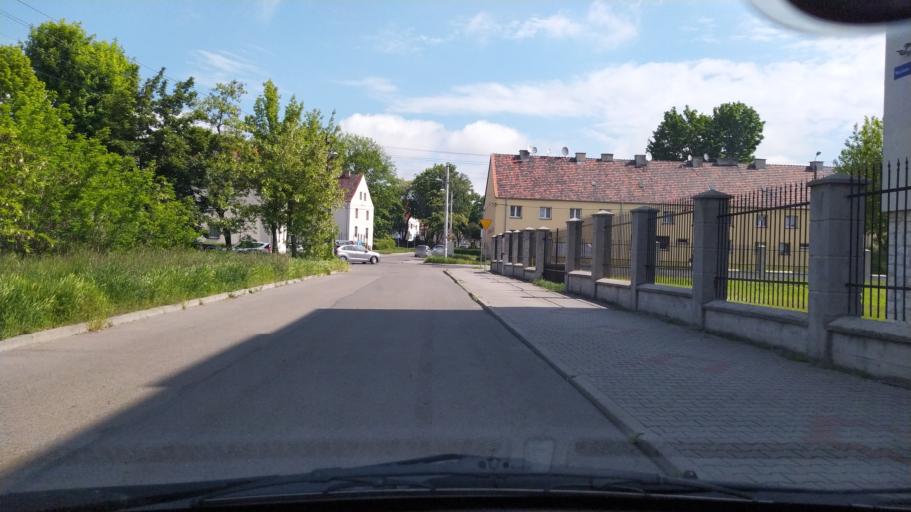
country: PL
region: Silesian Voivodeship
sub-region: Gliwice
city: Gliwice
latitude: 50.2892
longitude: 18.7207
